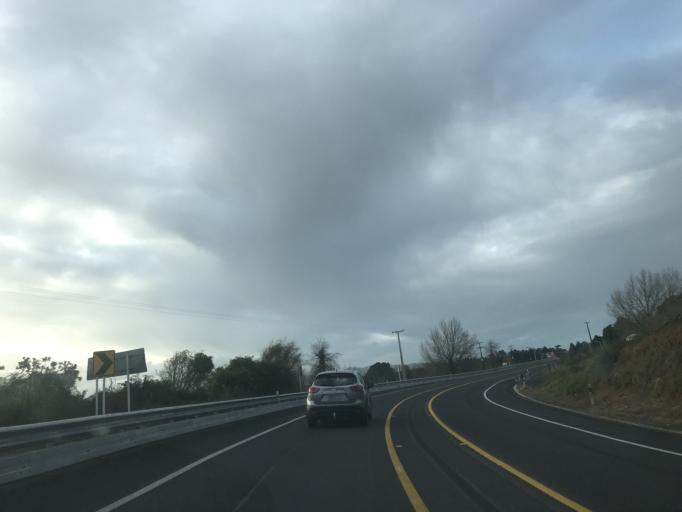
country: NZ
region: Waikato
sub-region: Hauraki District
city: Waihi
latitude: -37.4389
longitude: 175.8730
